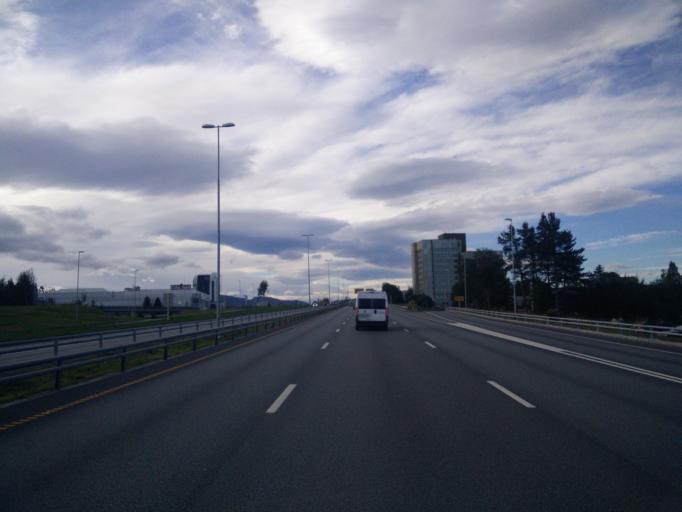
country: NO
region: Sor-Trondelag
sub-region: Trondheim
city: Trondheim
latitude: 63.3651
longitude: 10.3765
